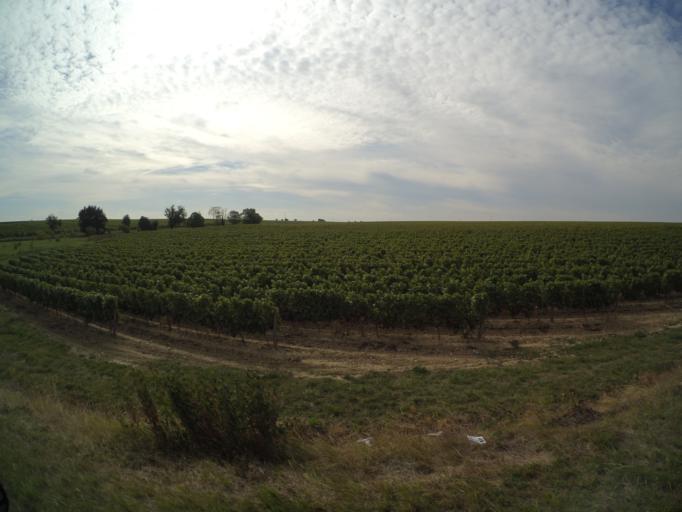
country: FR
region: Pays de la Loire
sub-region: Departement de Maine-et-Loire
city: Martigne-Briand
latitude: 47.2029
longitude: -0.4427
